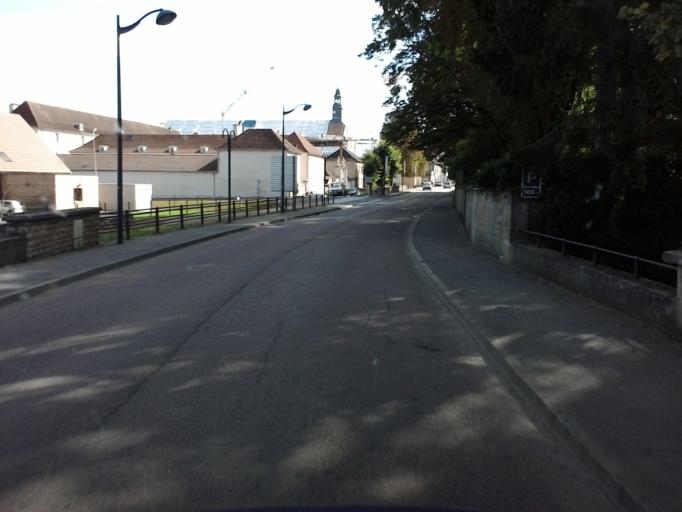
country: FR
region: Bourgogne
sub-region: Departement de la Cote-d'Or
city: Chatillon-sur-Seine
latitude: 47.8648
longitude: 4.5743
